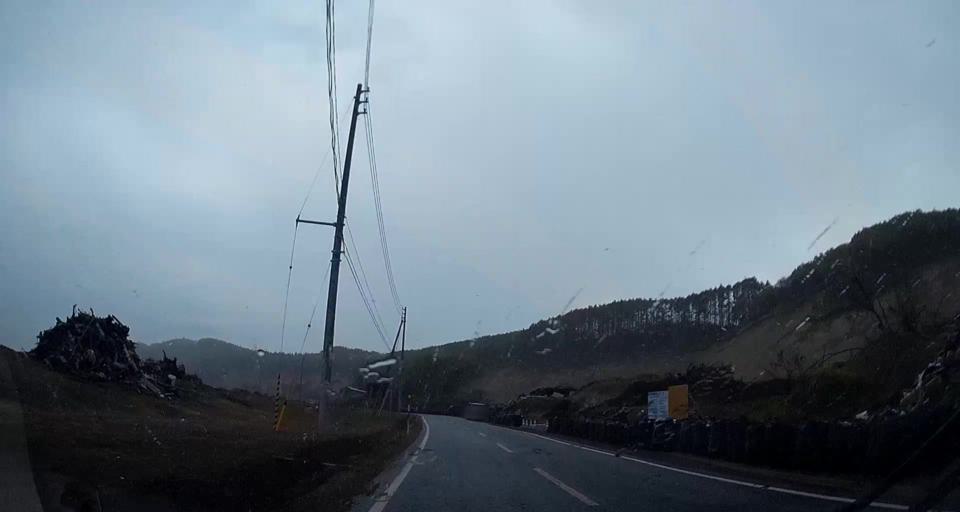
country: JP
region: Hokkaido
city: Chitose
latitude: 42.7496
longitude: 141.9120
